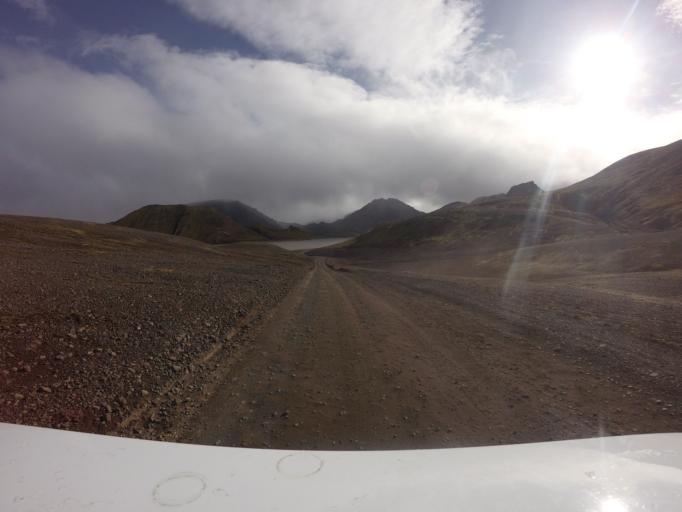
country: IS
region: South
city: Vestmannaeyjar
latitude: 64.0020
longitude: -18.9916
